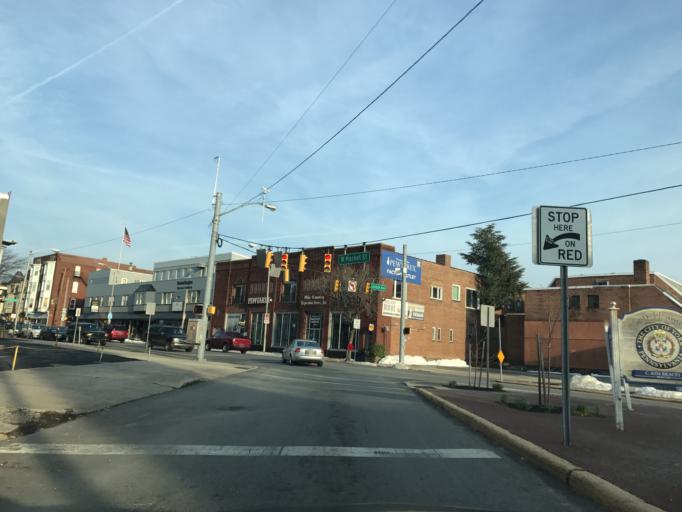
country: US
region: Pennsylvania
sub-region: York County
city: West York
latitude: 39.9569
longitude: -76.7465
